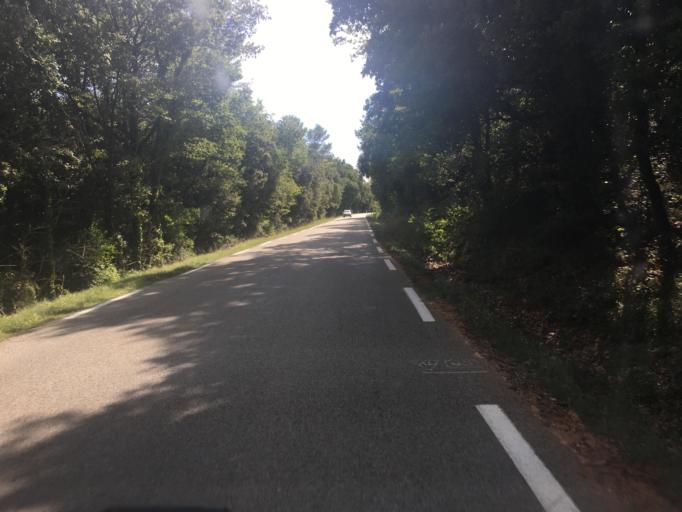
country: FR
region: Languedoc-Roussillon
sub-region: Departement du Gard
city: Connaux
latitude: 44.0458
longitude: 4.5675
